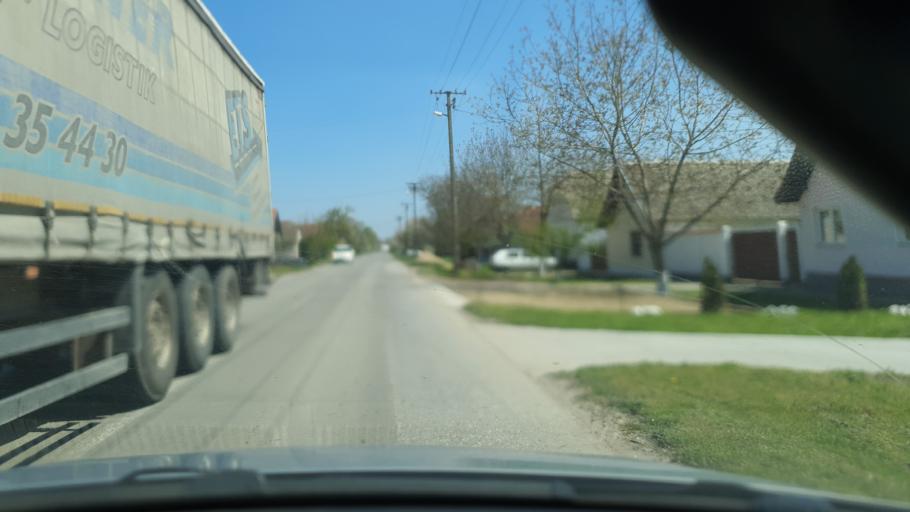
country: RS
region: Autonomna Pokrajina Vojvodina
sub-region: Zapadnobacki Okrug
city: Odzaci
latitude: 45.4582
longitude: 19.3258
